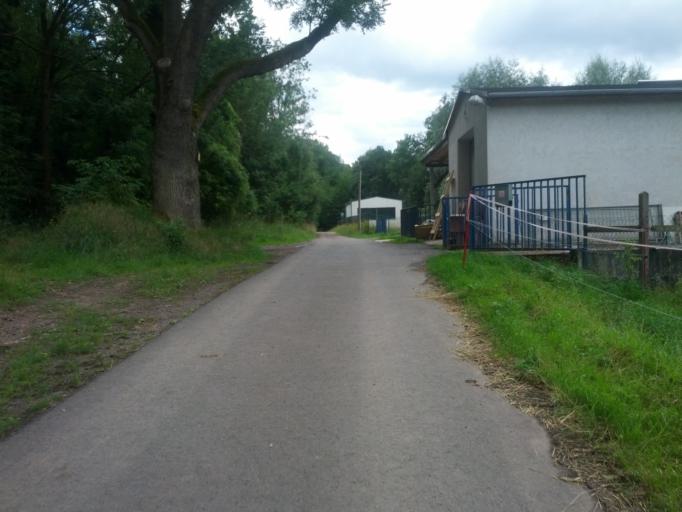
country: DE
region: Thuringia
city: Eisenach
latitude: 50.9875
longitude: 10.3755
